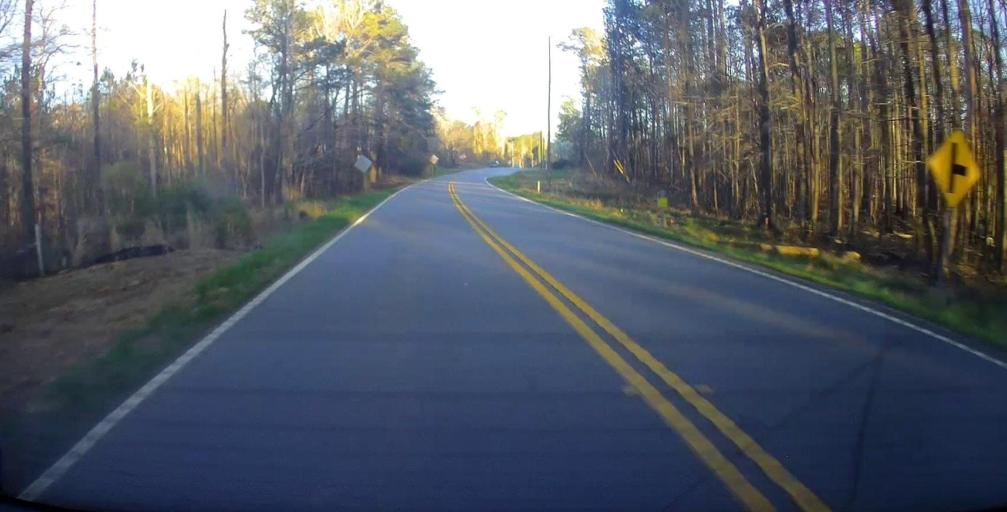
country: US
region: Georgia
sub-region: Harris County
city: Hamilton
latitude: 32.6678
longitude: -84.9680
